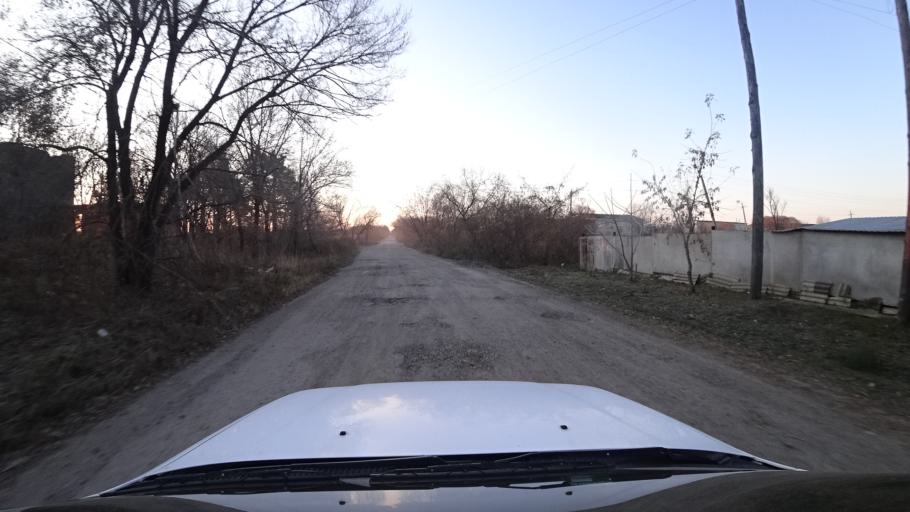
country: RU
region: Primorskiy
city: Dal'nerechensk
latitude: 45.9205
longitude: 133.7365
